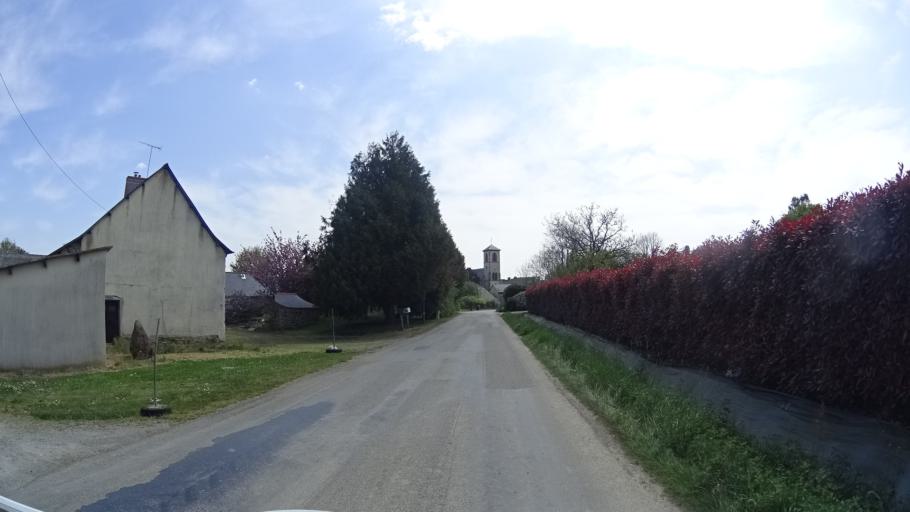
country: FR
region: Brittany
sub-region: Departement d'Ille-et-Vilaine
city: Torce
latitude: 48.0371
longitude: -1.2690
